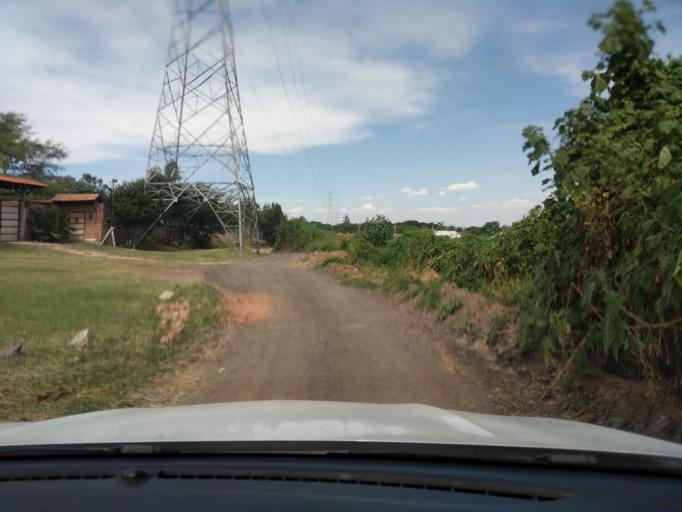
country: MX
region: Jalisco
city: Coyula
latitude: 20.6289
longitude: -103.2135
